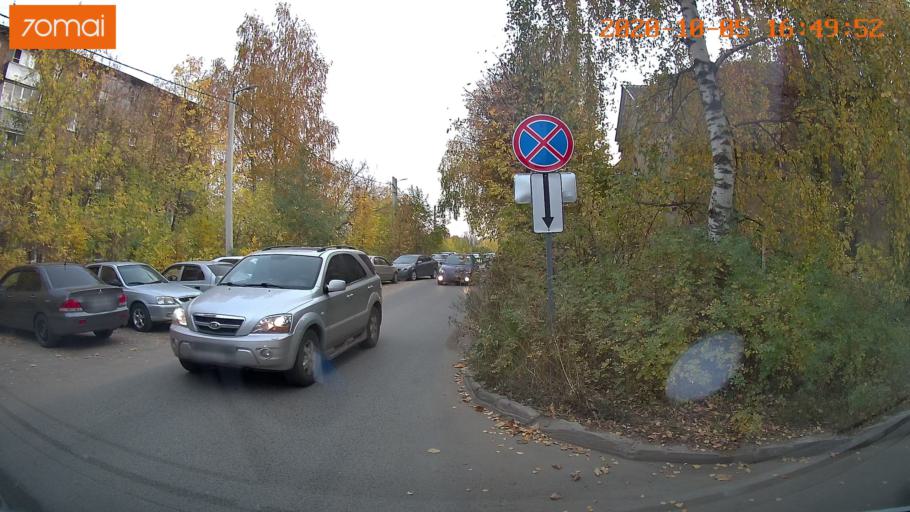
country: RU
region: Ivanovo
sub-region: Gorod Ivanovo
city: Ivanovo
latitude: 56.9658
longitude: 40.9777
